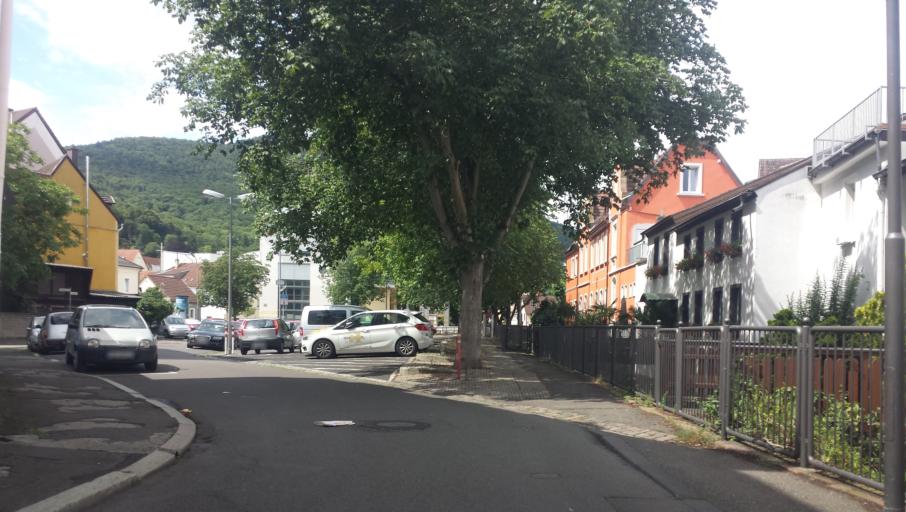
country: DE
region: Rheinland-Pfalz
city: Neustadt
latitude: 49.3532
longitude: 8.1330
